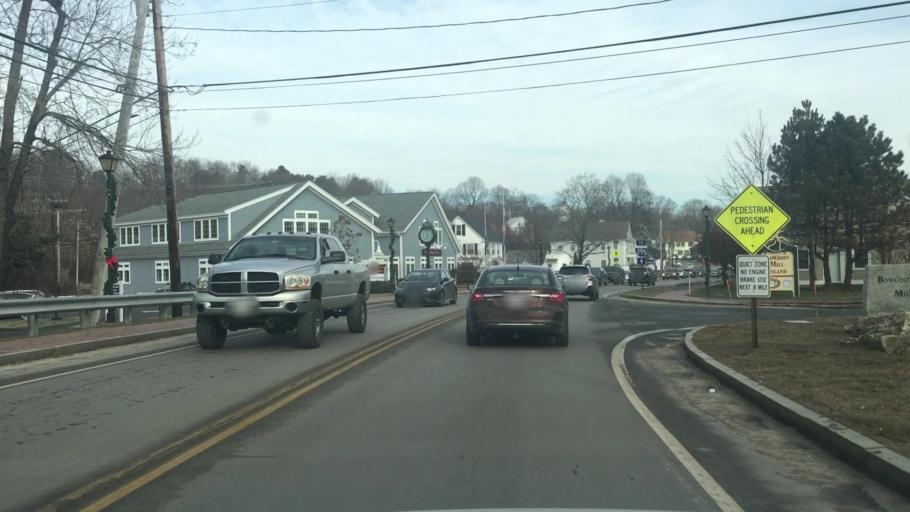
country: US
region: Maine
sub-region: Cumberland County
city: Brunswick
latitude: 43.9222
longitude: -69.9653
